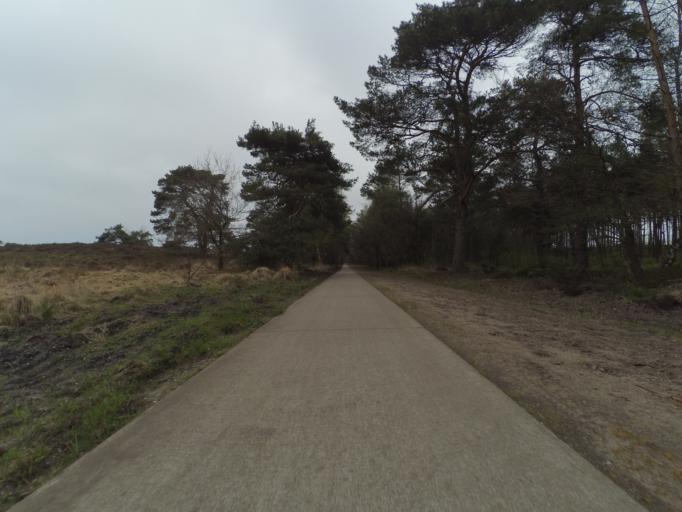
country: NL
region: Gelderland
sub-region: Gemeente Epe
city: Emst
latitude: 52.3424
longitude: 5.8789
